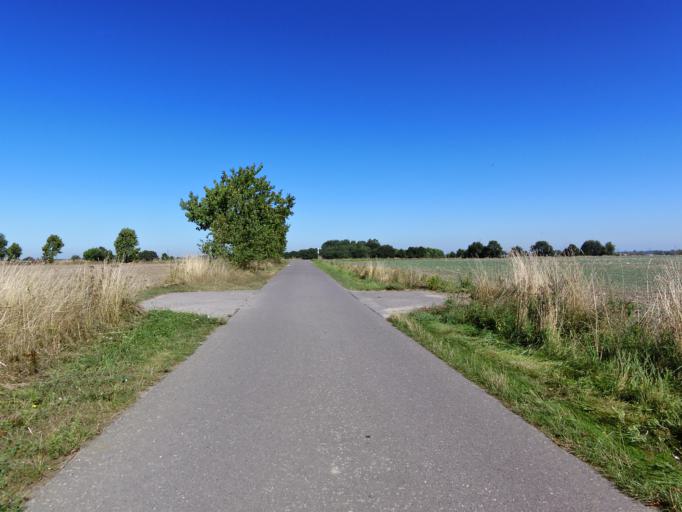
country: DE
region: Saxony
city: Dommitzsch
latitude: 51.6486
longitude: 12.8555
